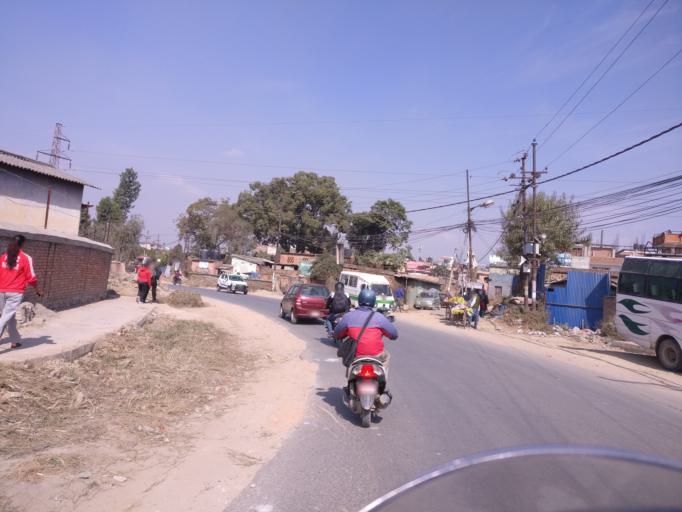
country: NP
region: Central Region
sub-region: Bagmati Zone
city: Patan
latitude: 27.6638
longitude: 85.3243
